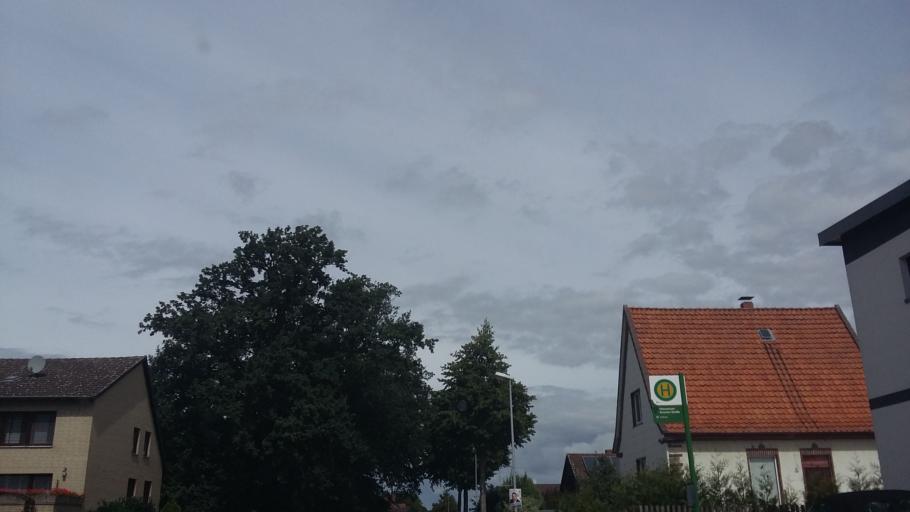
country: DE
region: Lower Saxony
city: Harsum
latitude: 52.1861
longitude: 10.0083
